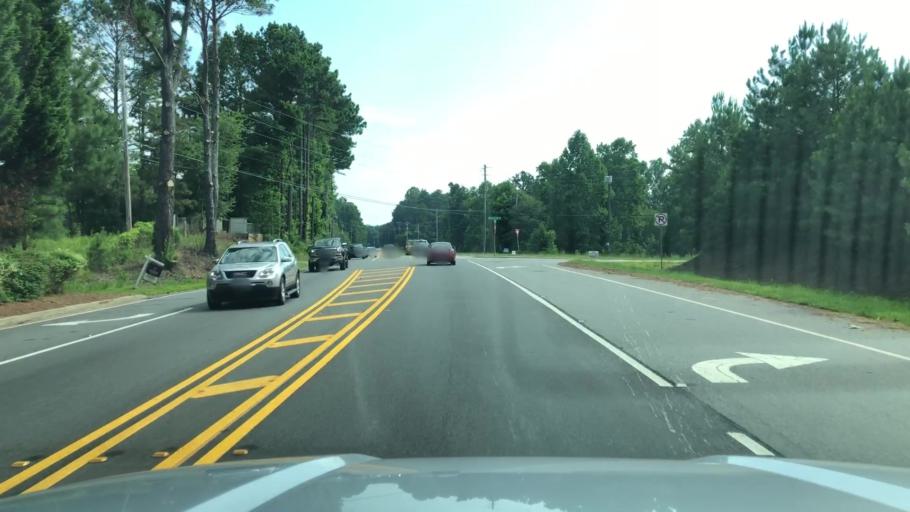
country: US
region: Georgia
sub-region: Cobb County
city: Acworth
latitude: 34.0440
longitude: -84.7293
